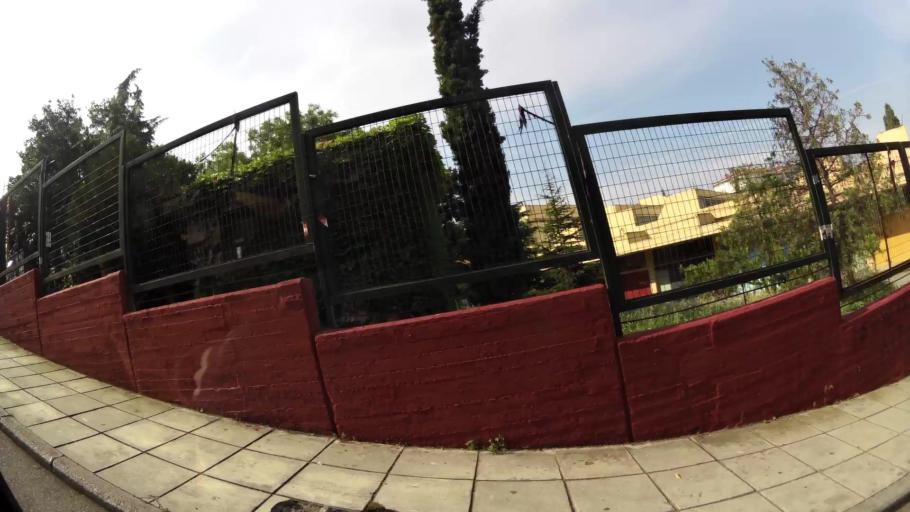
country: GR
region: Central Macedonia
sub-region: Nomos Thessalonikis
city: Polichni
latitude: 40.6577
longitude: 22.9434
